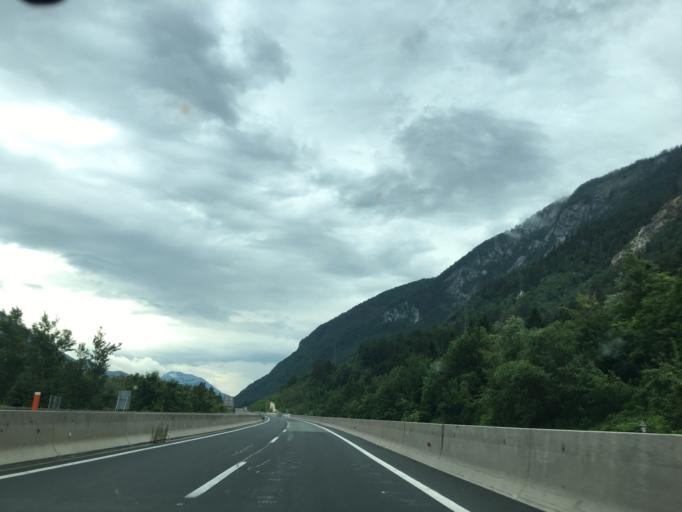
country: SI
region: Jesenice
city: Hrusica
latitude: 46.4354
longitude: 14.0414
